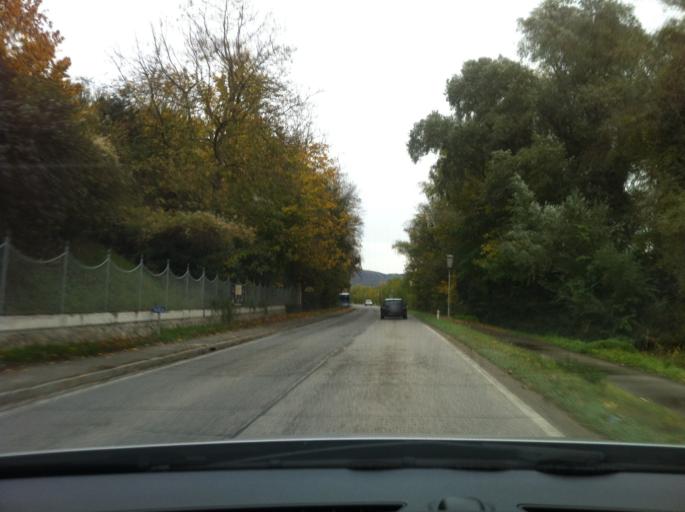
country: AT
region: Lower Austria
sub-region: Politischer Bezirk Melk
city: Emmersdorf an der Donau
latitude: 48.2376
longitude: 15.3288
